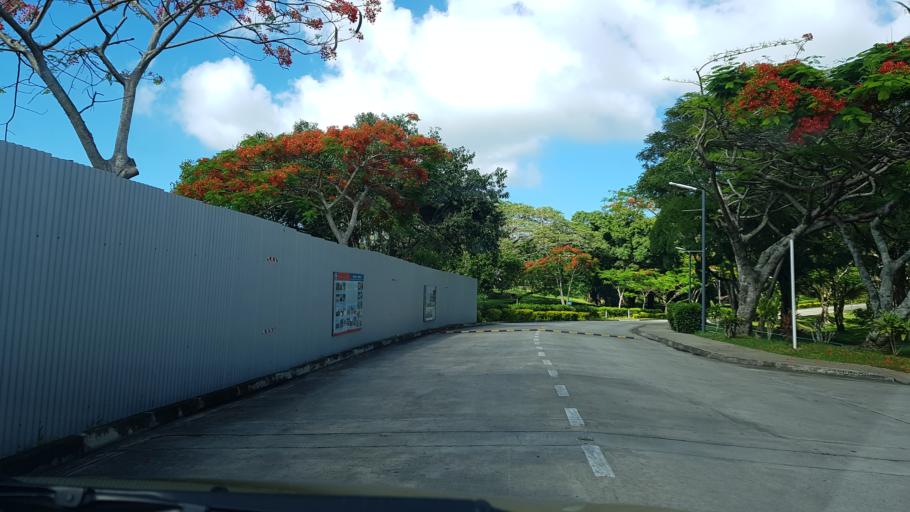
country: FJ
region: Central
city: Suva
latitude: -18.1513
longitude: 178.4458
